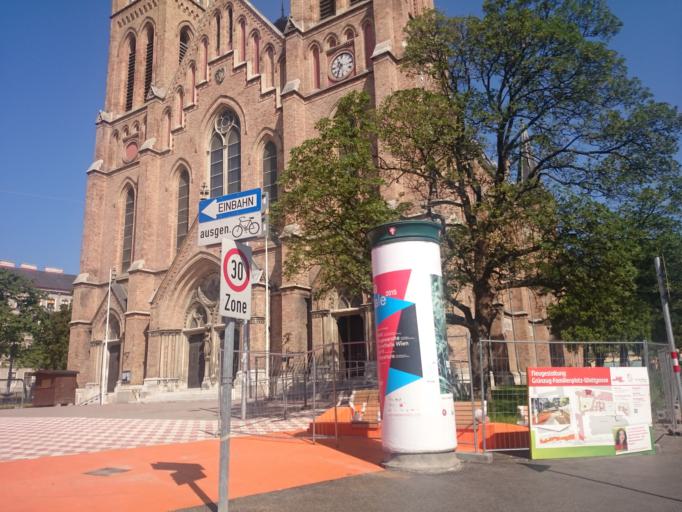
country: AT
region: Vienna
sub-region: Wien Stadt
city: Vienna
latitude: 48.2141
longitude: 16.3188
